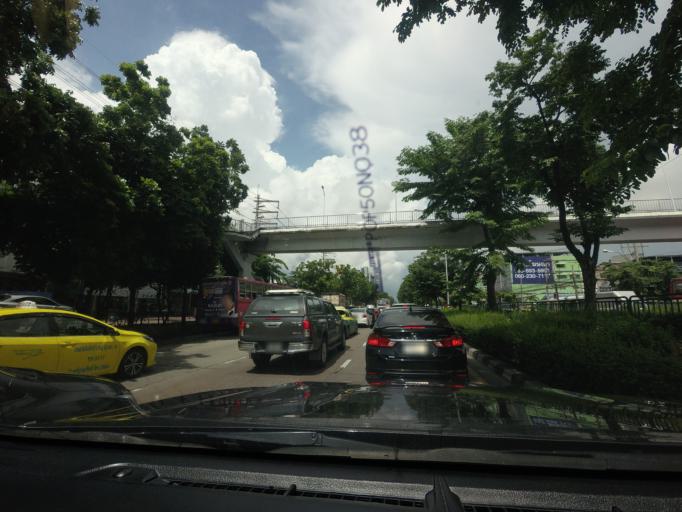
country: TH
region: Bangkok
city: Nong Khaem
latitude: 13.7082
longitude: 100.3783
